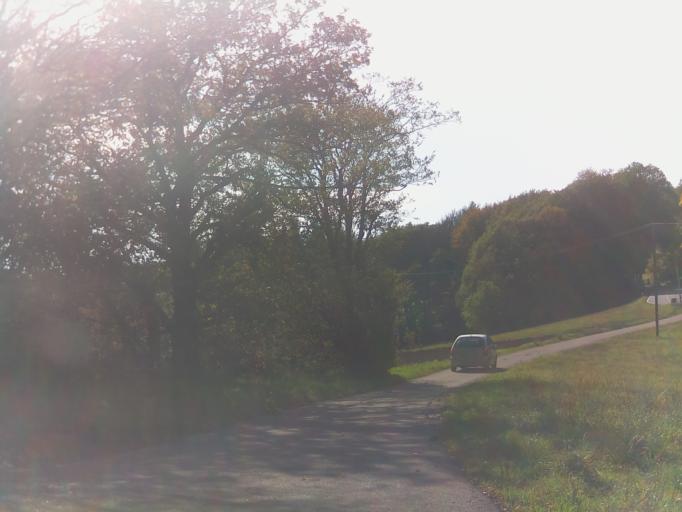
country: DE
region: Baden-Wuerttemberg
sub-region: Karlsruhe Region
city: Wilhelmsfeld
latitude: 49.4930
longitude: 8.7627
